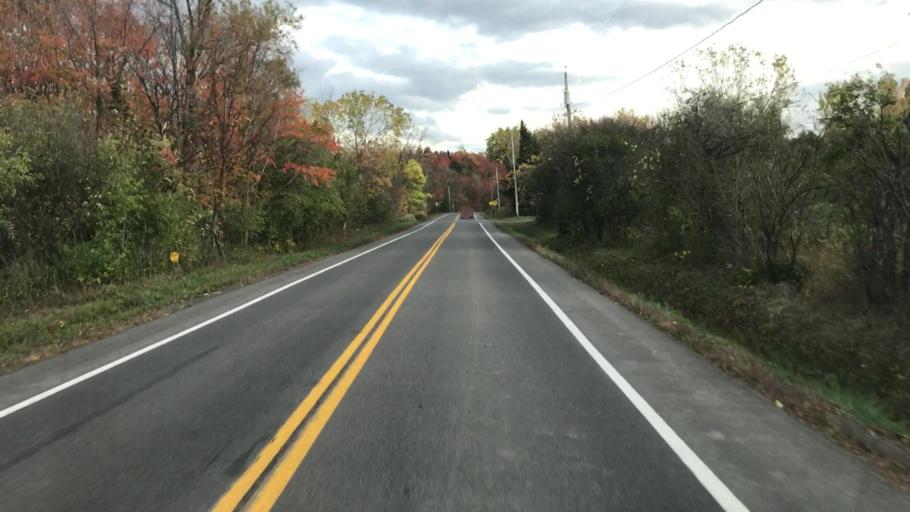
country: US
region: New York
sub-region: Onondaga County
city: Fayetteville
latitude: 42.9843
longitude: -76.0417
